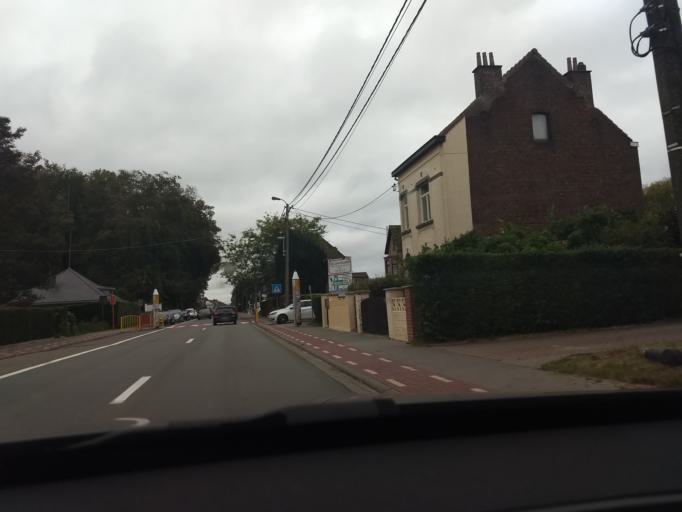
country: BE
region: Wallonia
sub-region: Province du Brabant Wallon
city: Braine-l'Alleud
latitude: 50.6747
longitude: 4.3832
